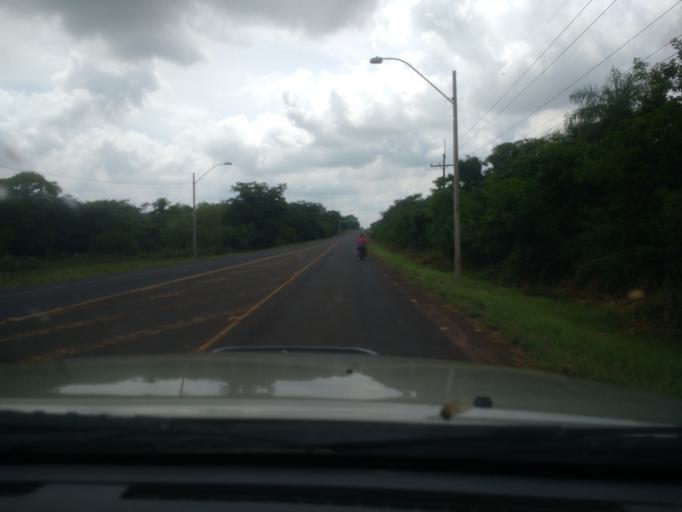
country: PY
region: San Pedro
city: Puerto Rosario
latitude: -24.4247
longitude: -57.0837
